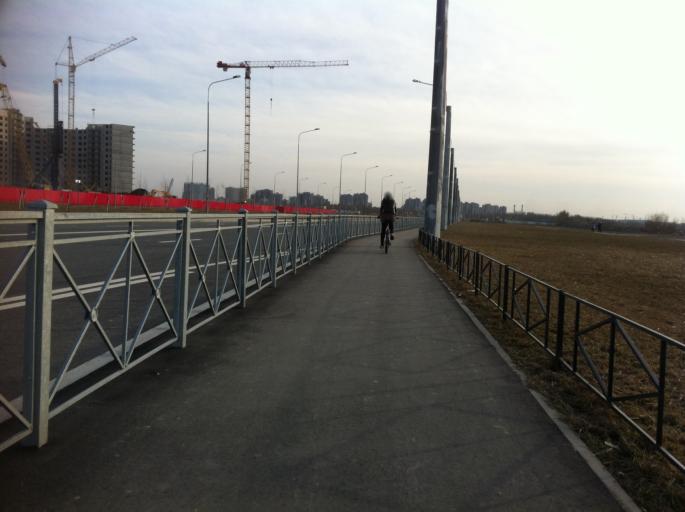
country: RU
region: St.-Petersburg
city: Sosnovaya Polyana
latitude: 59.8705
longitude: 30.1554
